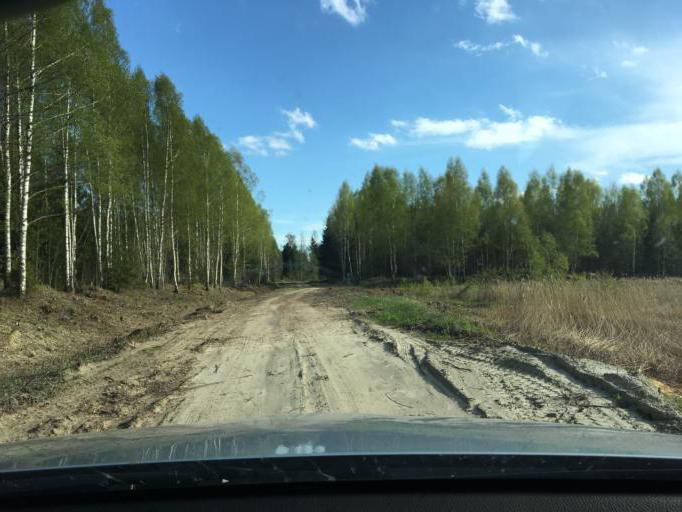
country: LV
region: Ozolnieku
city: Ozolnieki
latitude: 56.6627
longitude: 23.8665
